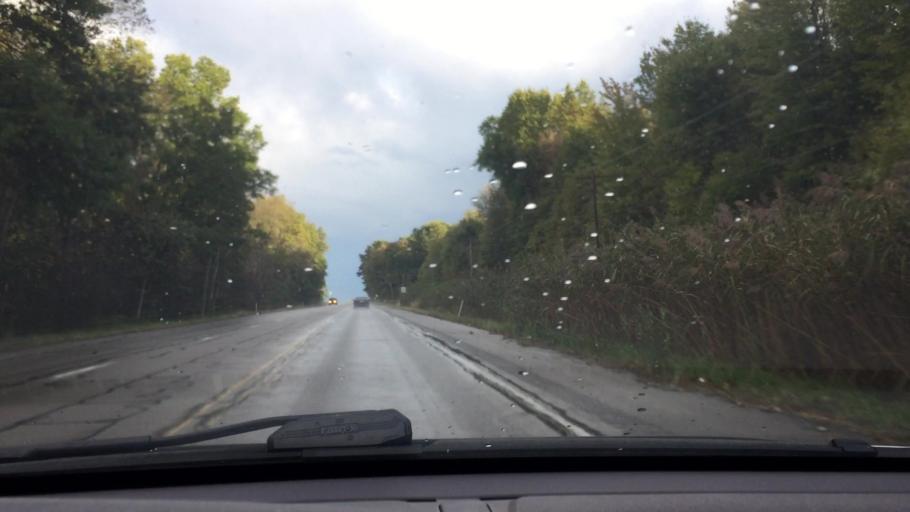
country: US
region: Ohio
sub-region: Mahoning County
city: Lowellville
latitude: 41.0636
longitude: -80.4589
